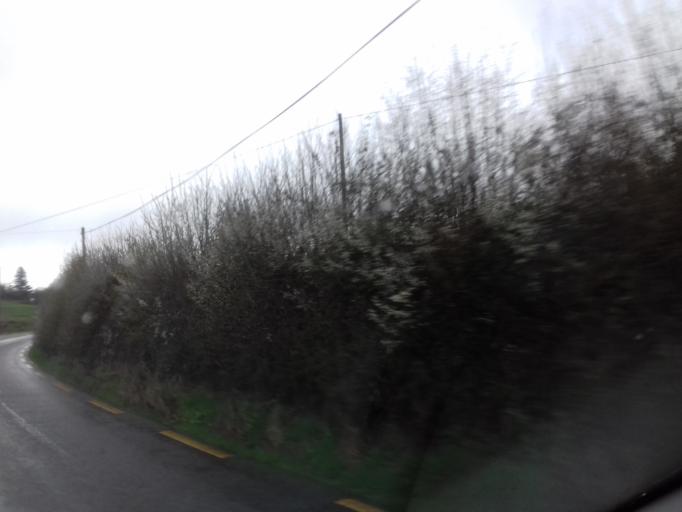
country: IE
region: Connaught
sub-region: County Leitrim
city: Manorhamilton
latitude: 54.2737
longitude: -7.9372
